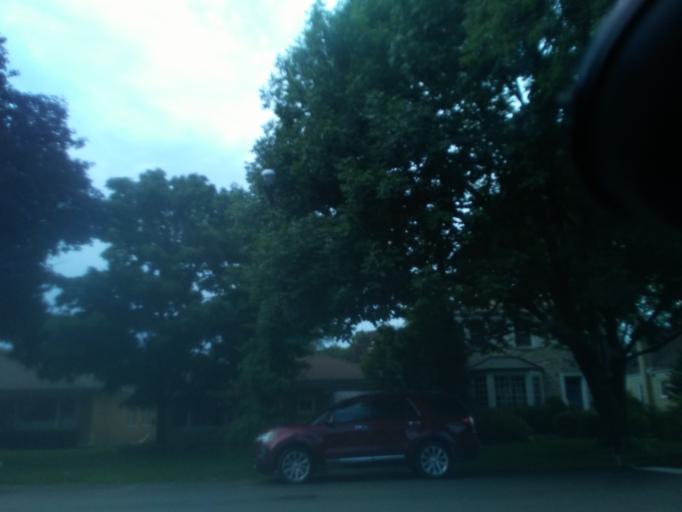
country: US
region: Illinois
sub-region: Cook County
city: Lincolnwood
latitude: 41.9899
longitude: -87.7553
